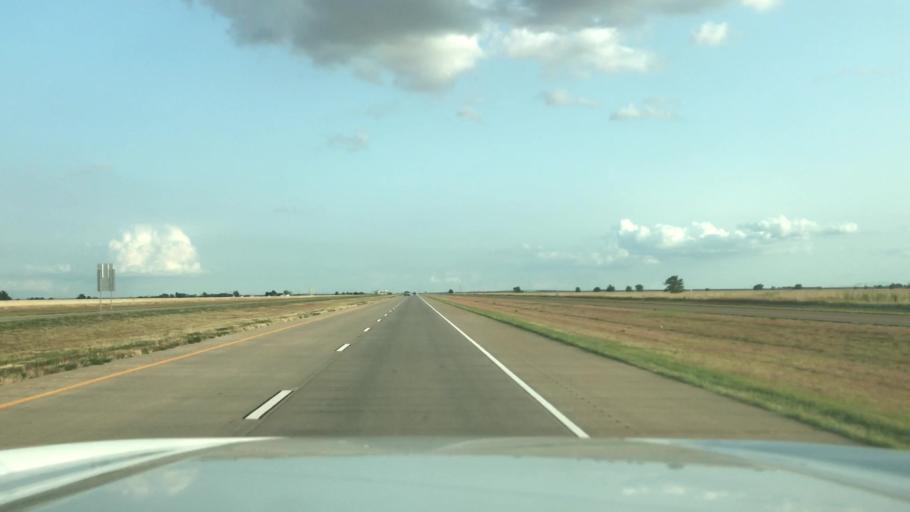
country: US
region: Texas
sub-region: Swisher County
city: Tulia
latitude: 34.5106
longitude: -101.7914
